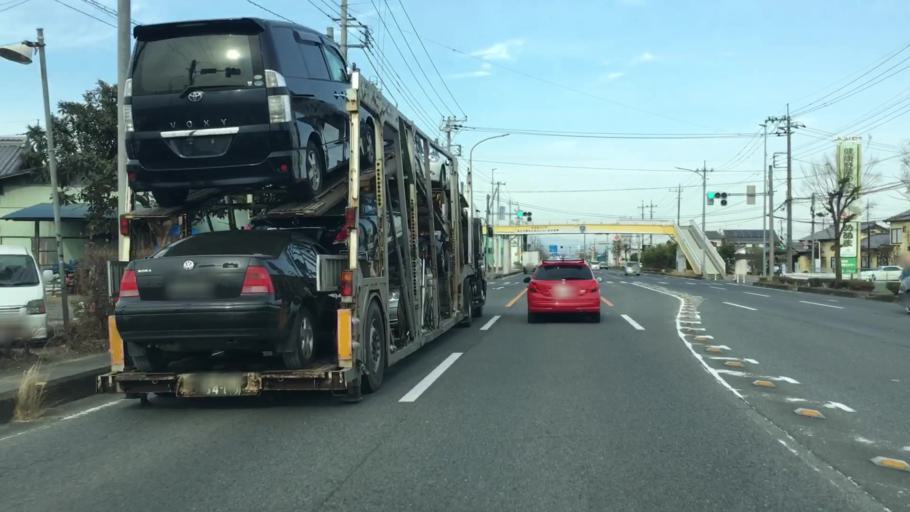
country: JP
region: Saitama
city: Menuma
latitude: 36.2223
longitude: 139.3688
